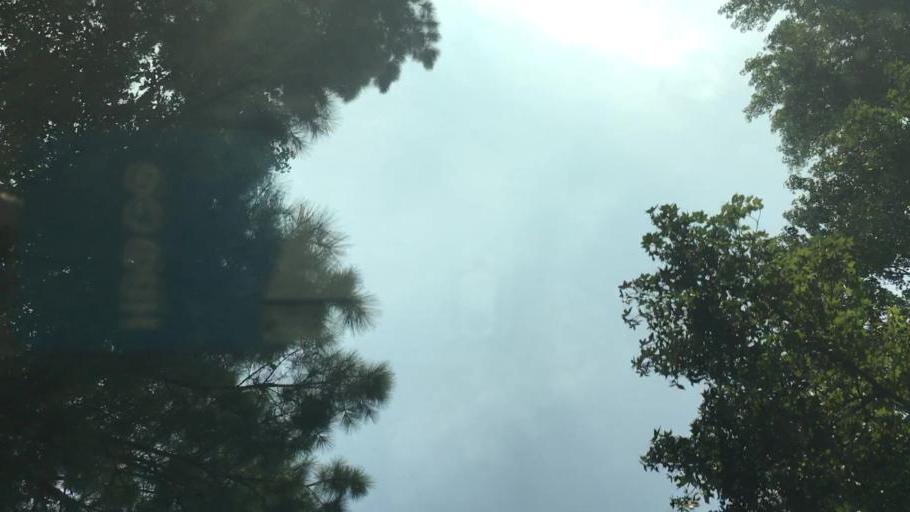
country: US
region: Alabama
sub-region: Bibb County
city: Woodstock
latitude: 33.2136
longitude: -87.0854
